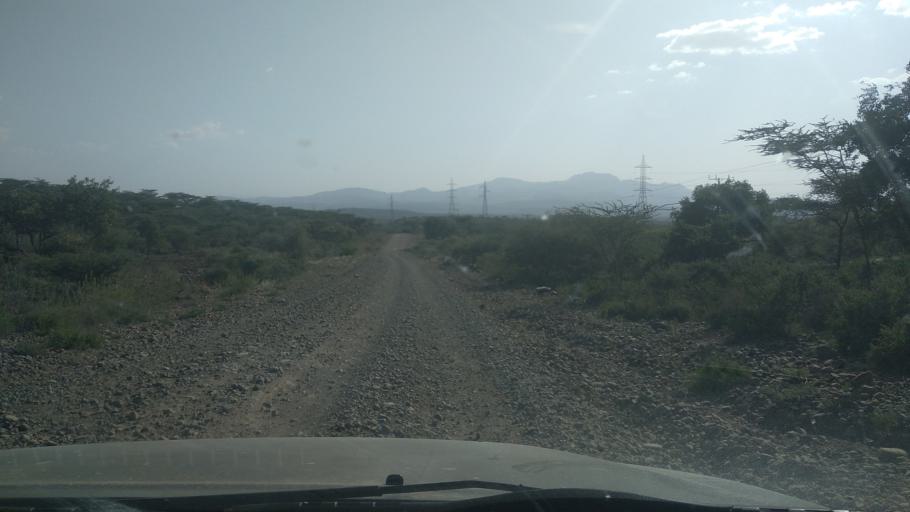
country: ET
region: Oromiya
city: Hirna
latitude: 9.5007
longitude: 41.0408
